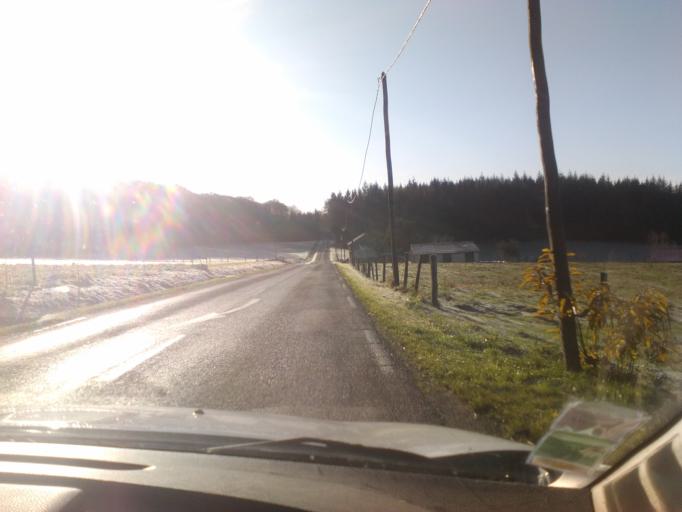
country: FR
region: Lorraine
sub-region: Departement des Vosges
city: Xertigny
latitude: 48.0320
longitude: 6.4189
